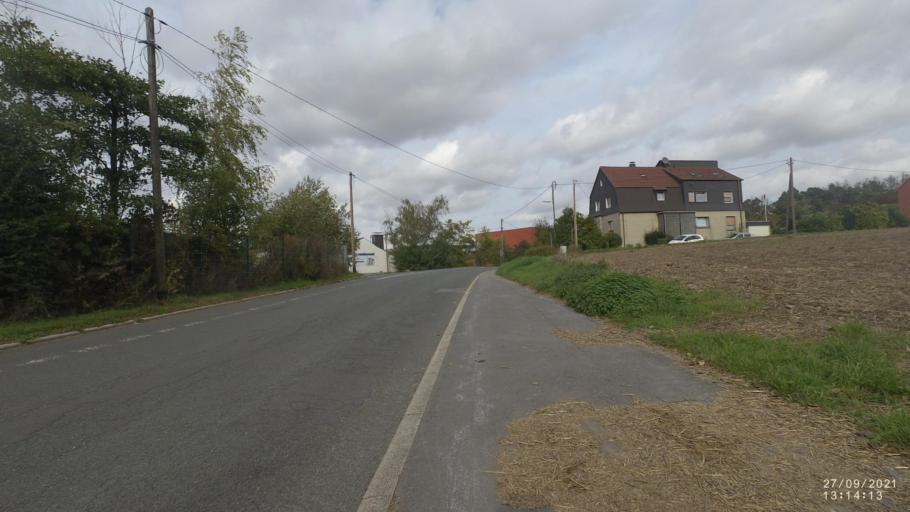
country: DE
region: North Rhine-Westphalia
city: Iserlohn
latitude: 51.4284
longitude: 7.6830
